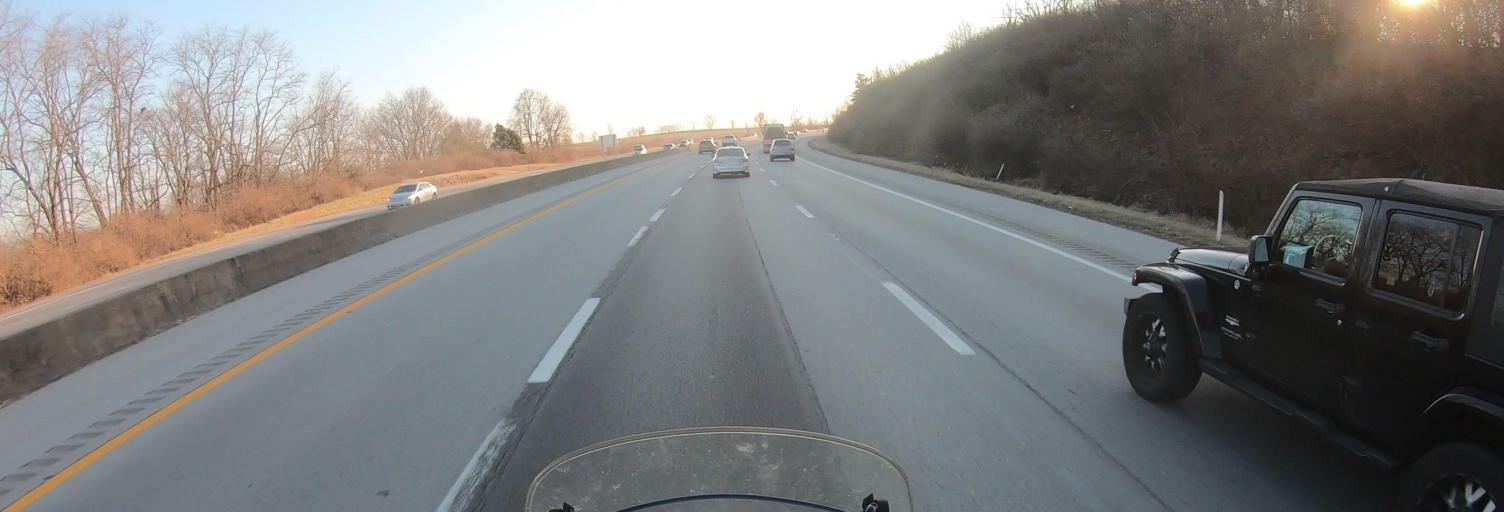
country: US
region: Kentucky
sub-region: Scott County
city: Georgetown
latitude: 38.1931
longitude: -84.5253
